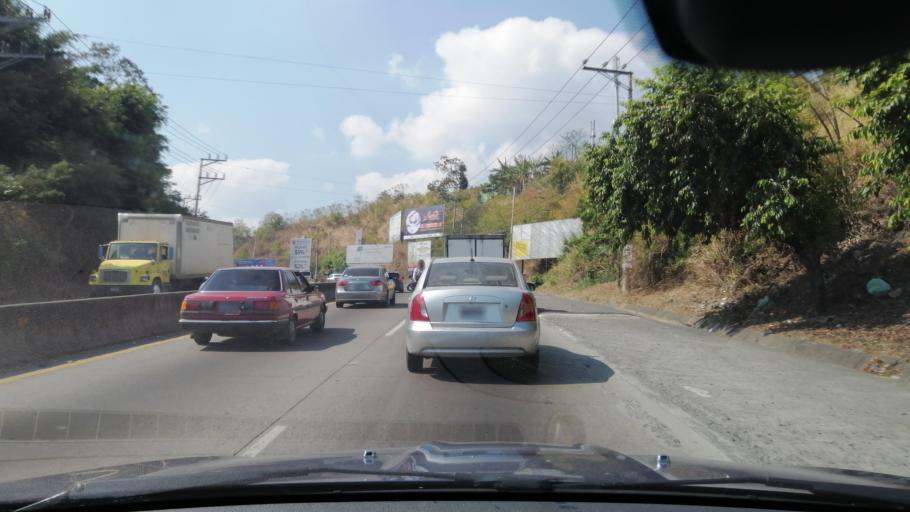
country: SV
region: San Salvador
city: Mejicanos
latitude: 13.7468
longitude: -89.2190
